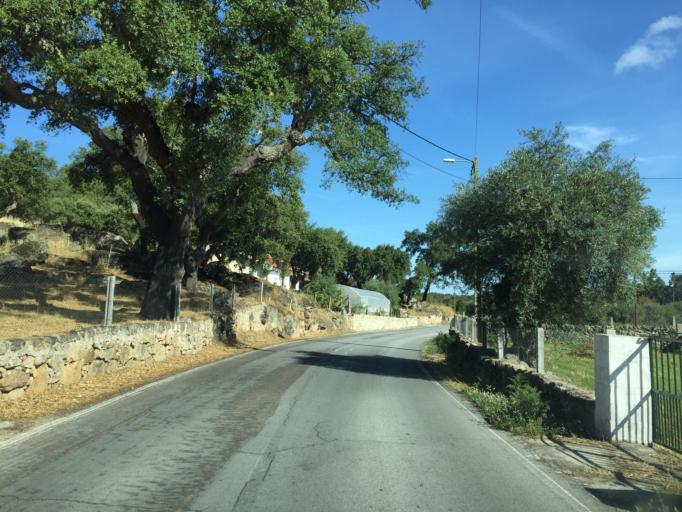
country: PT
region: Portalegre
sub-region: Marvao
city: Marvao
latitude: 39.4192
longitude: -7.3523
